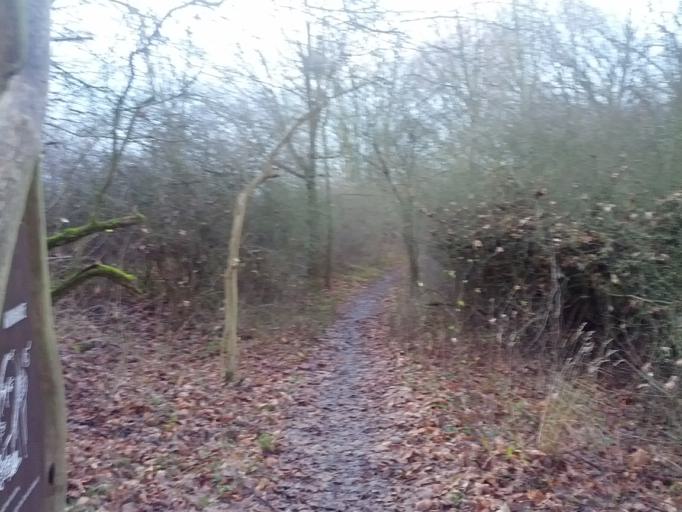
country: DE
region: Thuringia
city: Bischofroda
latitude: 51.0509
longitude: 10.4014
